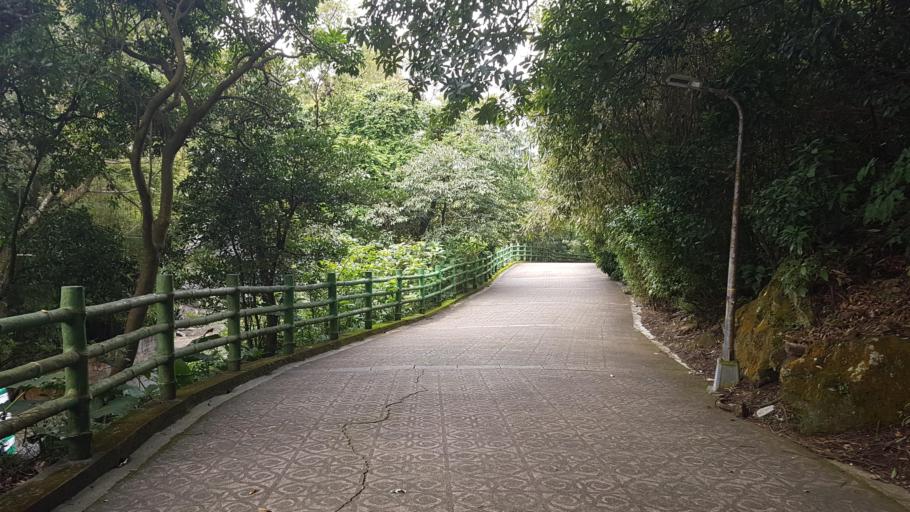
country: TW
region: Taipei
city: Taipei
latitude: 25.1524
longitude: 121.5401
